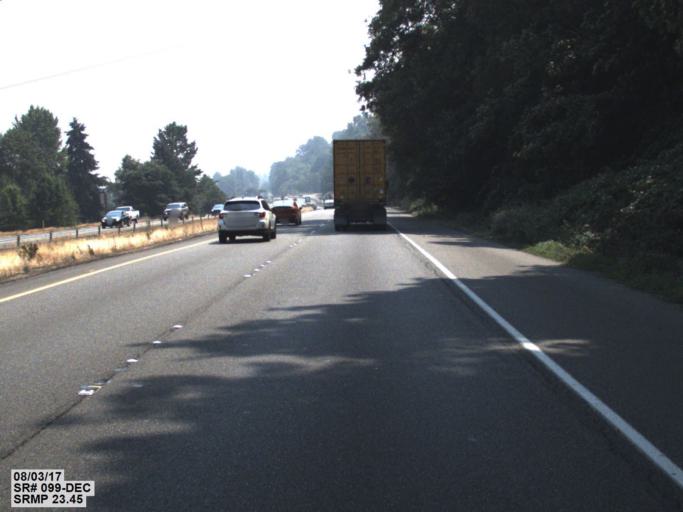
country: US
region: Washington
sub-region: King County
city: Riverton
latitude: 47.5042
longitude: -122.2994
